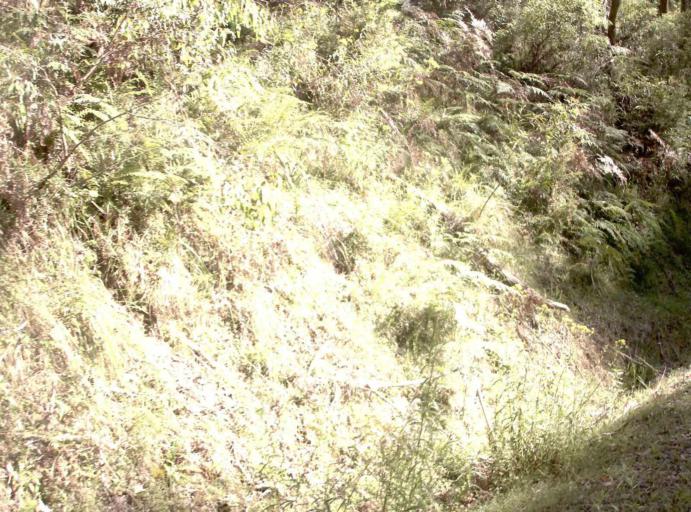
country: AU
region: New South Wales
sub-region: Bombala
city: Bombala
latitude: -37.3532
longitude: 148.6910
